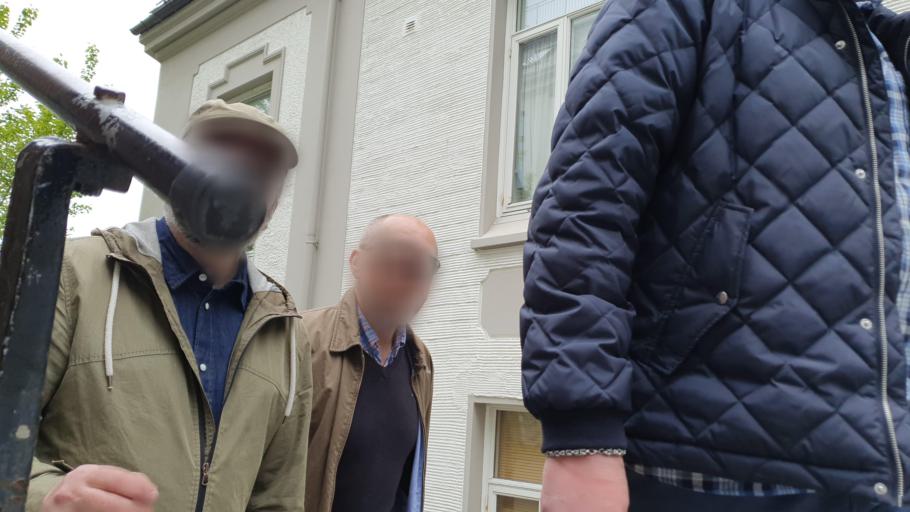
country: NO
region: More og Romsdal
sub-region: Alesund
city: Alesund
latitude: 62.4733
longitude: 6.1566
